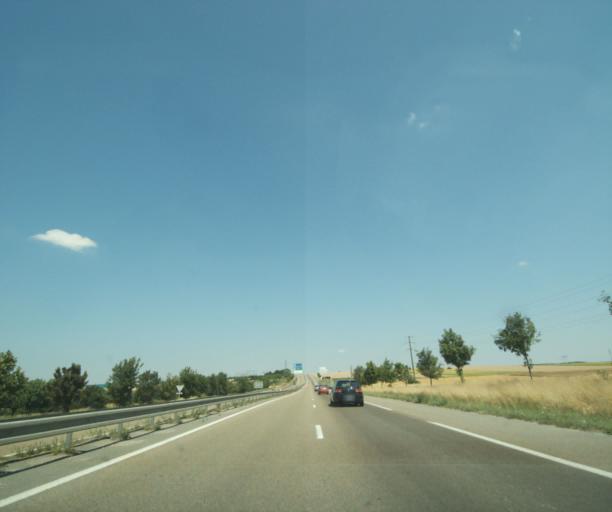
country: FR
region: Champagne-Ardenne
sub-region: Departement de la Marne
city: Fagnieres
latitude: 48.9888
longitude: 4.3474
